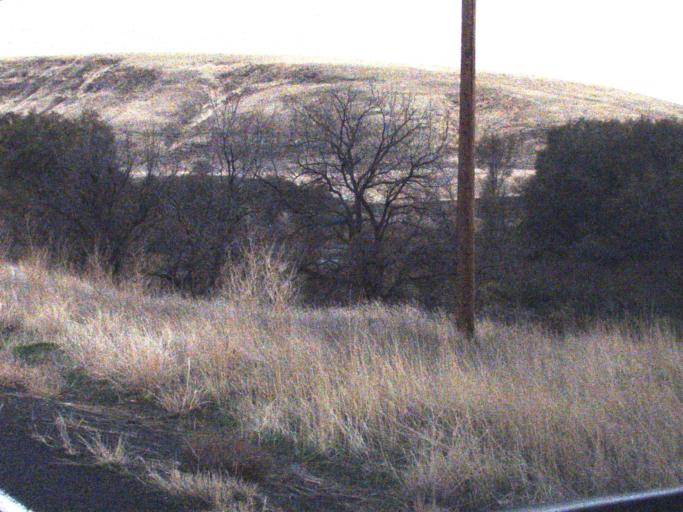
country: US
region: Washington
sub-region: Columbia County
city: Dayton
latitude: 46.5062
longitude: -118.0452
